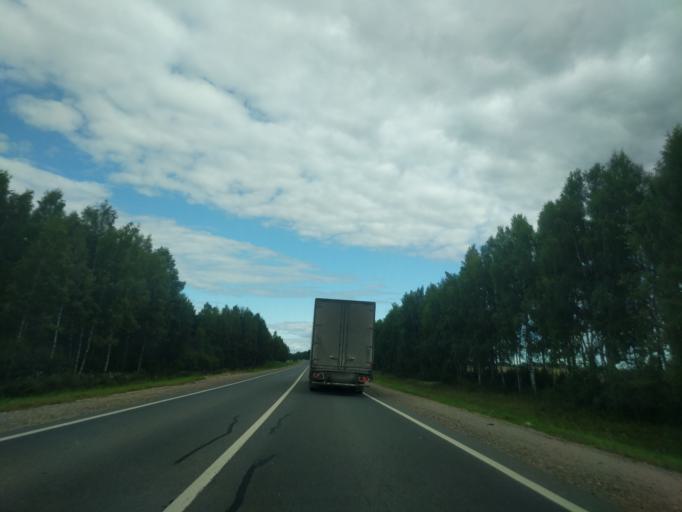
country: RU
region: Kostroma
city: Ostrovskoye
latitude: 57.8159
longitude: 42.2132
